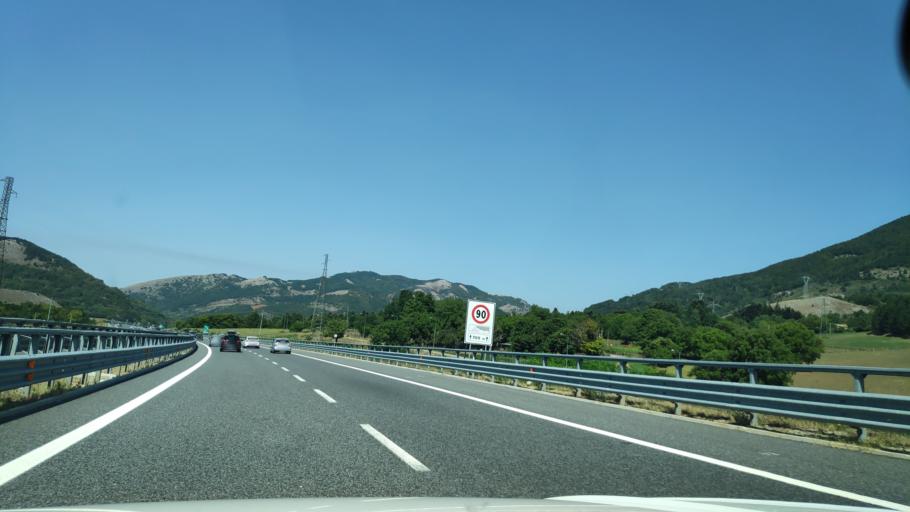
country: IT
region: Calabria
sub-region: Provincia di Cosenza
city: Mormanno
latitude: 39.8763
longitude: 16.0671
